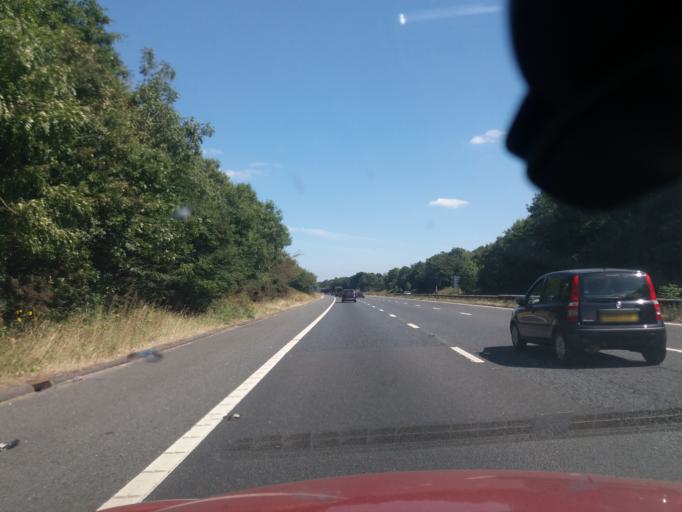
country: GB
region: England
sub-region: Borough of Wigan
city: Atherton
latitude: 53.5516
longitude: -2.4786
